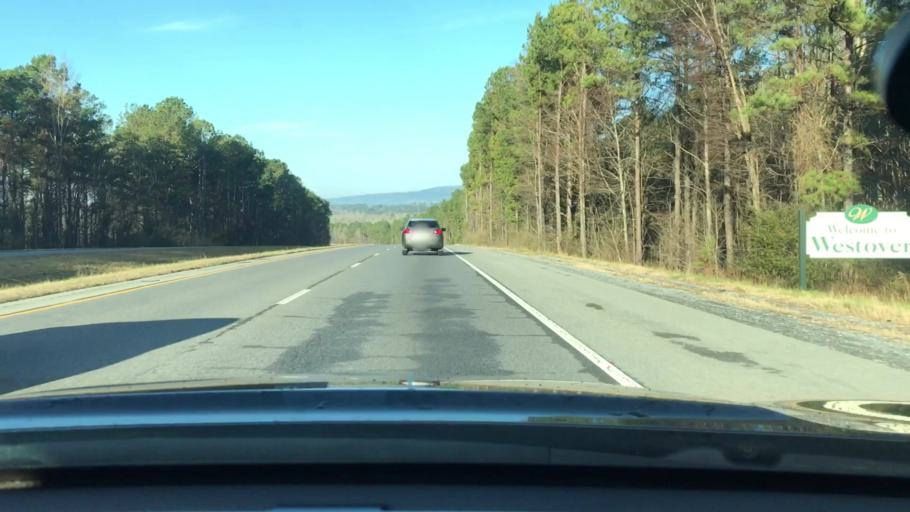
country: US
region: Alabama
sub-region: Shelby County
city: Harpersville
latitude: 33.3552
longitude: -86.4849
